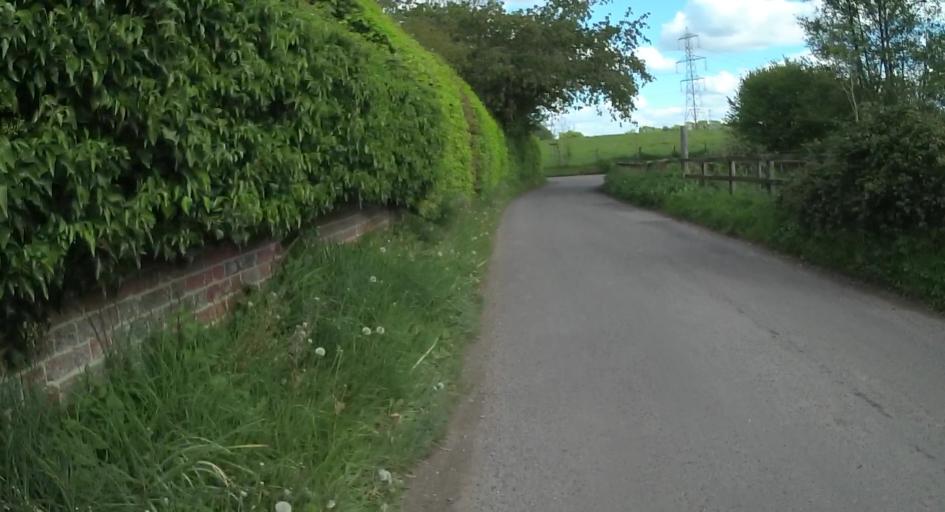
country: GB
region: England
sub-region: West Berkshire
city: Stratfield Mortimer
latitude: 51.3497
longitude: -1.0663
